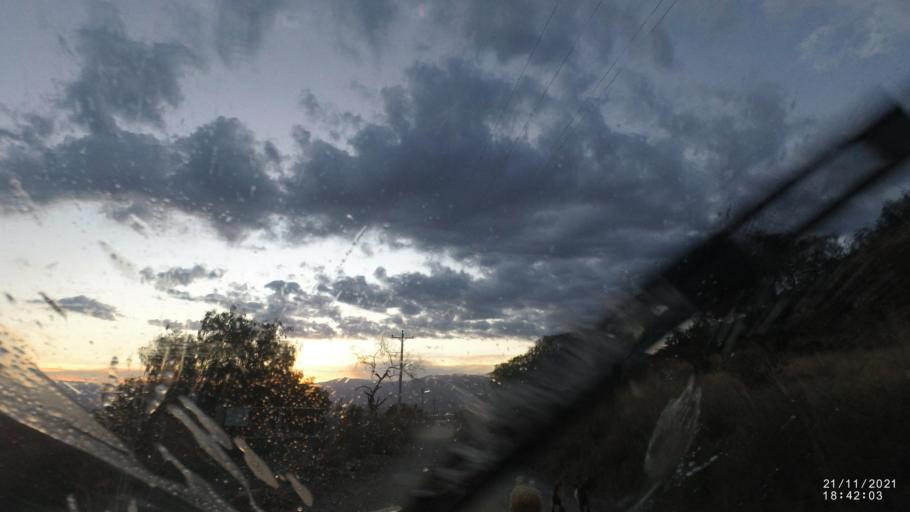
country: BO
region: Cochabamba
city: Cochabamba
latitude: -17.3196
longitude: -66.2165
